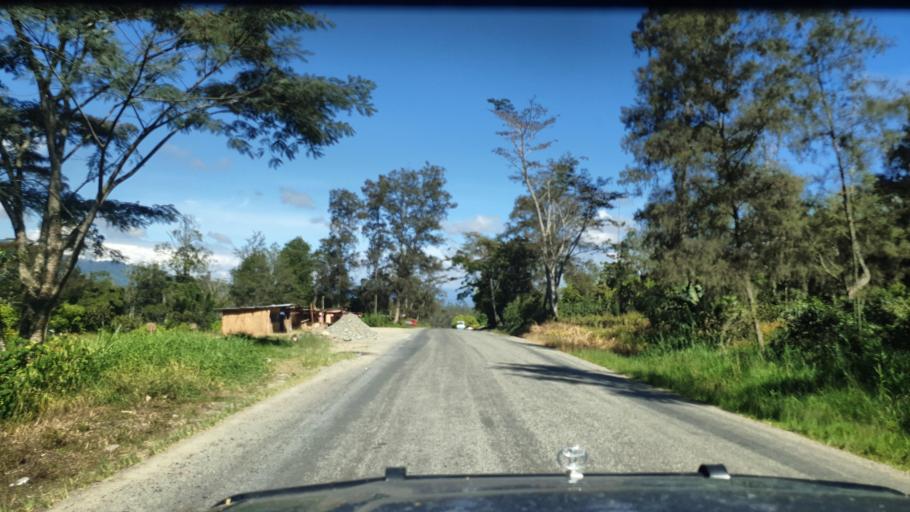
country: PG
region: Western Highlands
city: Rauna
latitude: -5.8328
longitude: 144.3599
